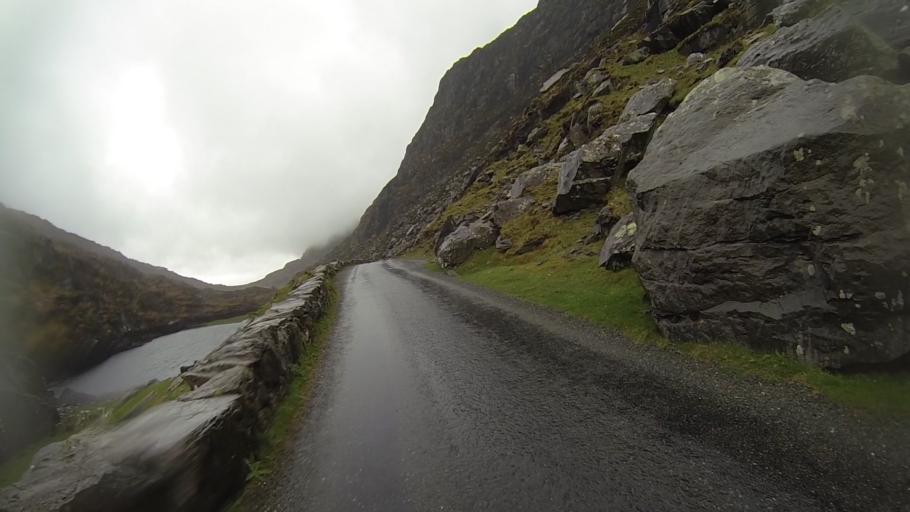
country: IE
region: Munster
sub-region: Ciarrai
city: Cill Airne
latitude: 52.0066
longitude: -9.6424
